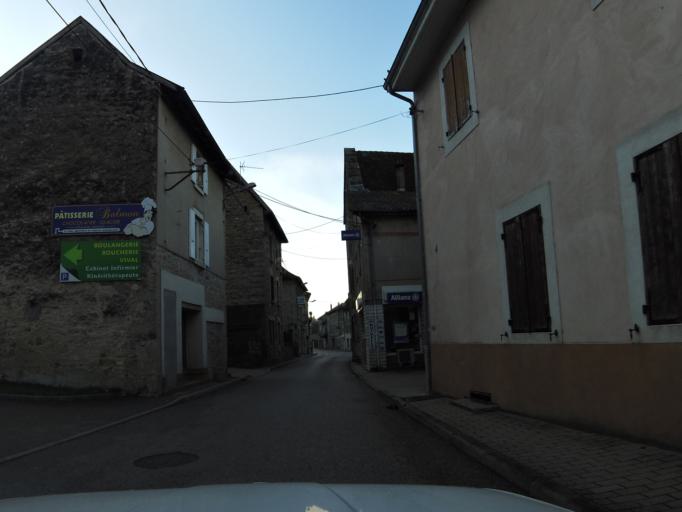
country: FR
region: Rhone-Alpes
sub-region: Departement de l'Isere
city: Bouvesse-Quirieu
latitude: 45.8077
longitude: 5.4535
